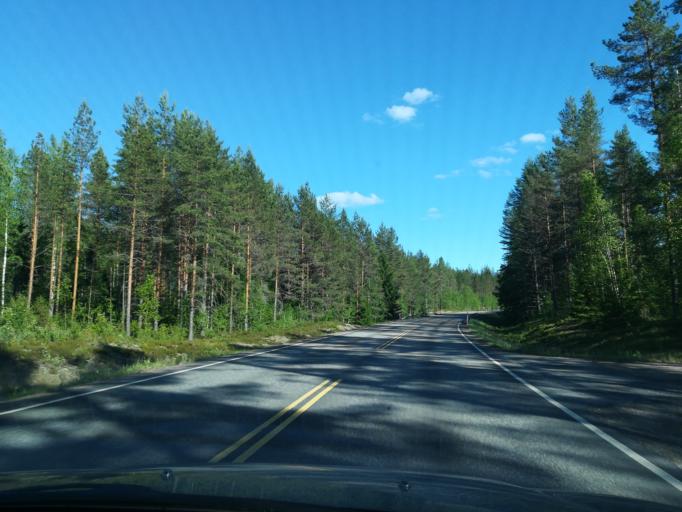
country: FI
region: South Karelia
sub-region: Imatra
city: Ruokolahti
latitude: 61.3982
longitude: 28.6308
